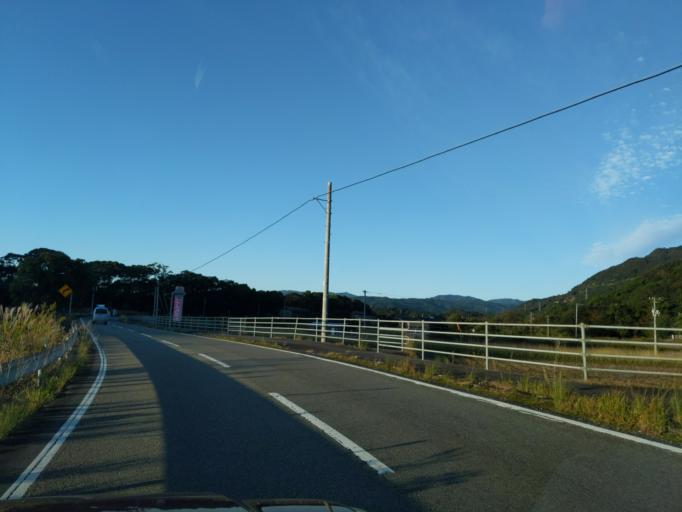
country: JP
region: Kochi
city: Muroto-misakicho
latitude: 33.5842
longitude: 134.3305
